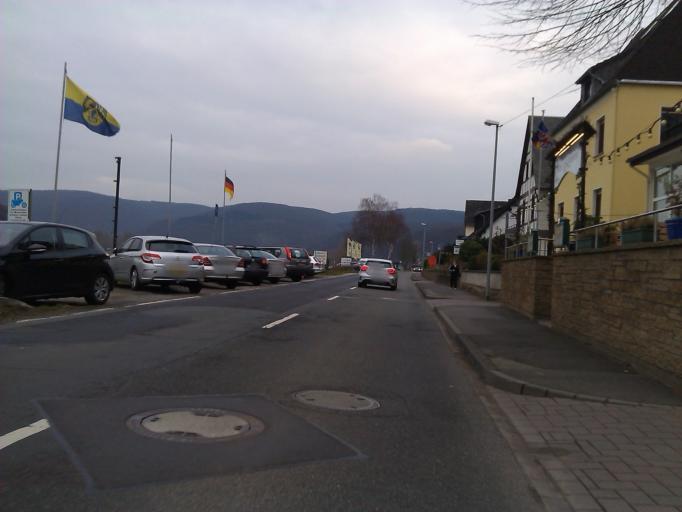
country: DE
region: Rheinland-Pfalz
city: Osterspai
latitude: 50.2462
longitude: 7.6170
